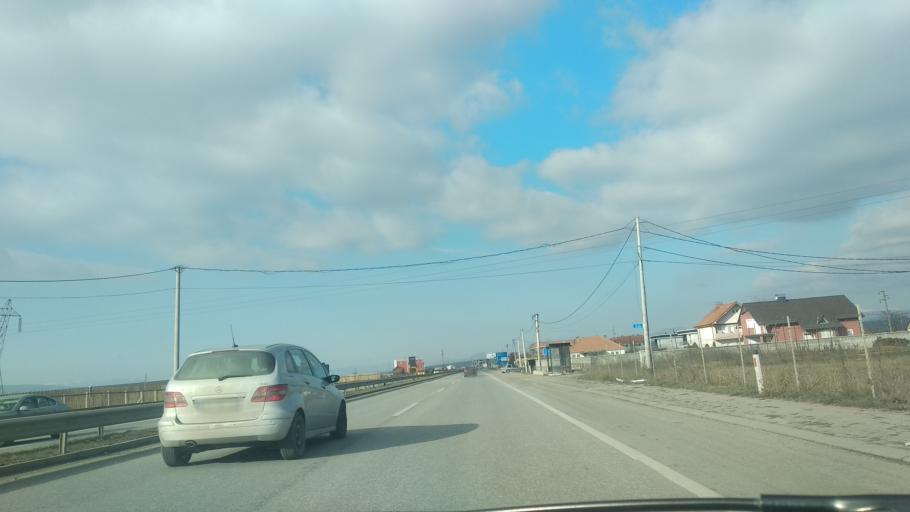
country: XK
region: Pristina
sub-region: Komuna e Obiliqit
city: Obiliq
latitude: 42.7086
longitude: 21.1039
